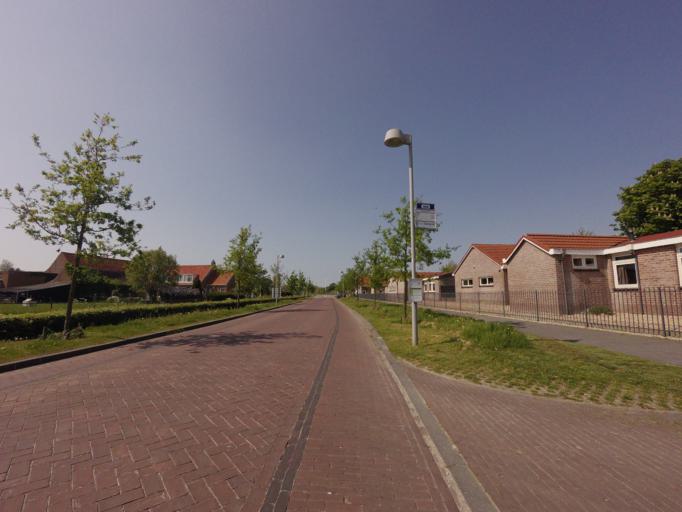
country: NL
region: Zeeland
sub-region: Gemeente Middelburg
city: Middelburg
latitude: 51.5538
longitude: 3.5873
